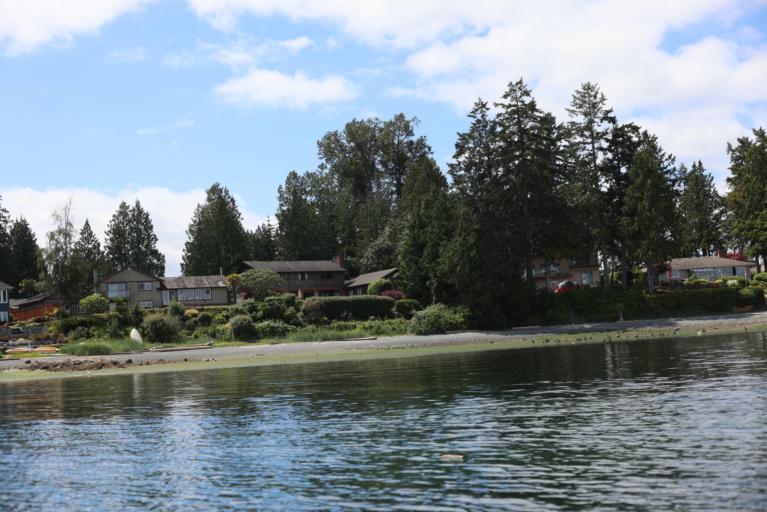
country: CA
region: British Columbia
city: North Saanich
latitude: 48.6009
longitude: -123.3905
